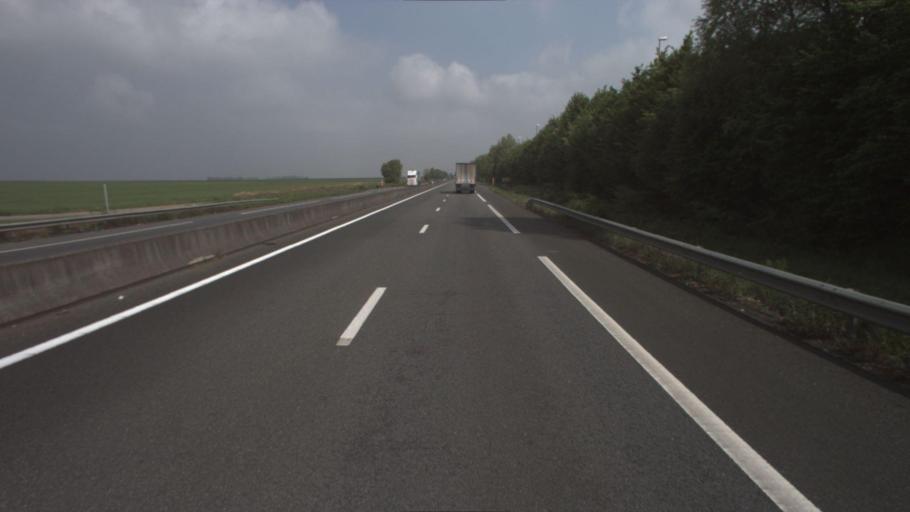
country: FR
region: Picardie
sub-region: Departement de l'Oise
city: Lagny-le-Sec
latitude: 49.0877
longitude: 2.7327
